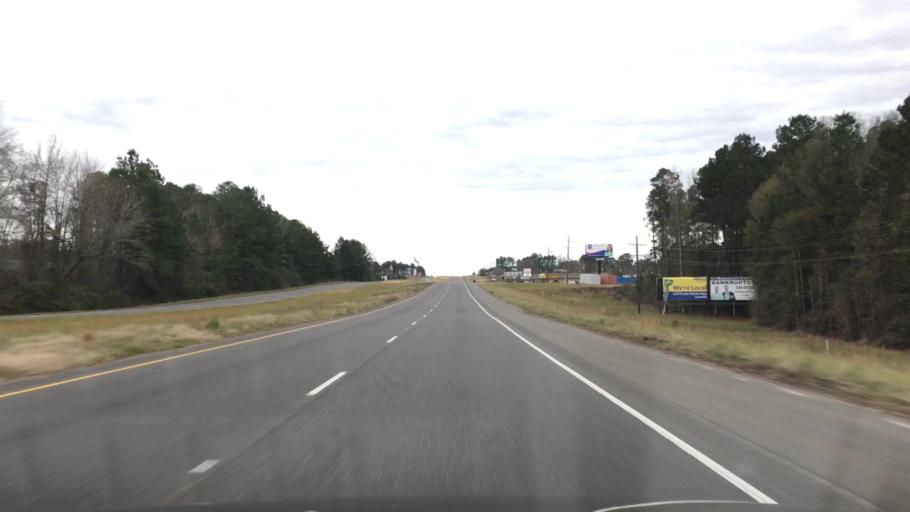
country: US
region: Louisiana
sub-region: Vernon Parish
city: New Llano
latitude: 31.0976
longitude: -93.2696
